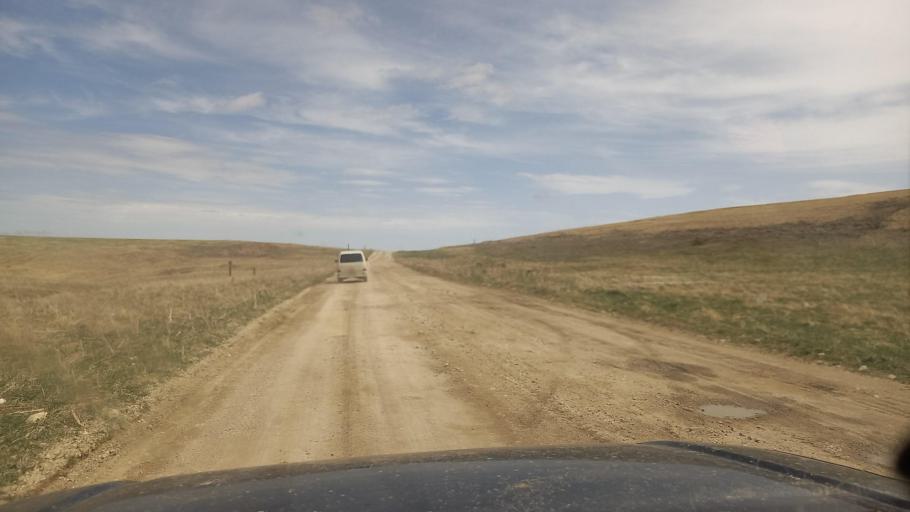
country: RU
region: Stavropol'skiy
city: Kislovodsk
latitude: 43.7494
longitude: 42.7069
